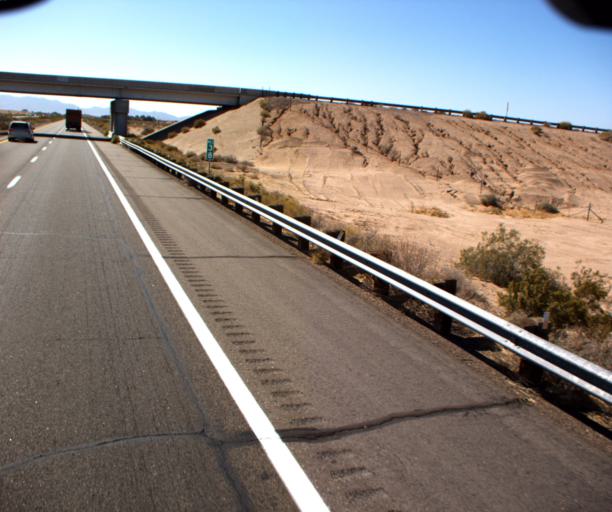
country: US
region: Arizona
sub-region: Yuma County
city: Wellton
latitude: 32.6819
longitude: -114.0212
